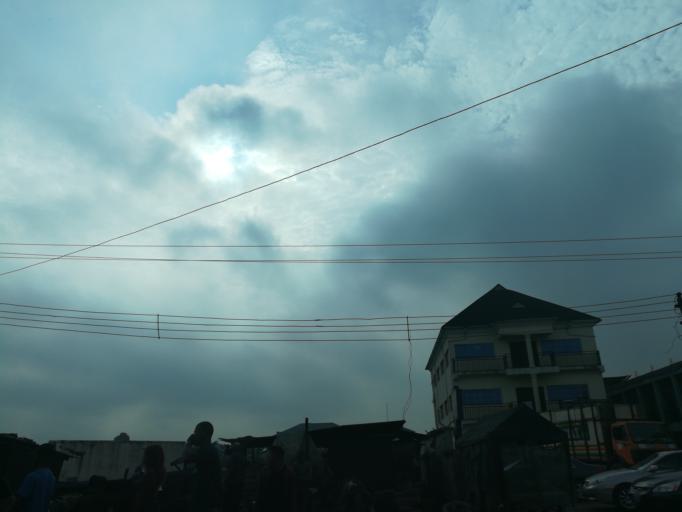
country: NG
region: Rivers
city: Port Harcourt
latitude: 4.8019
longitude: 6.9958
